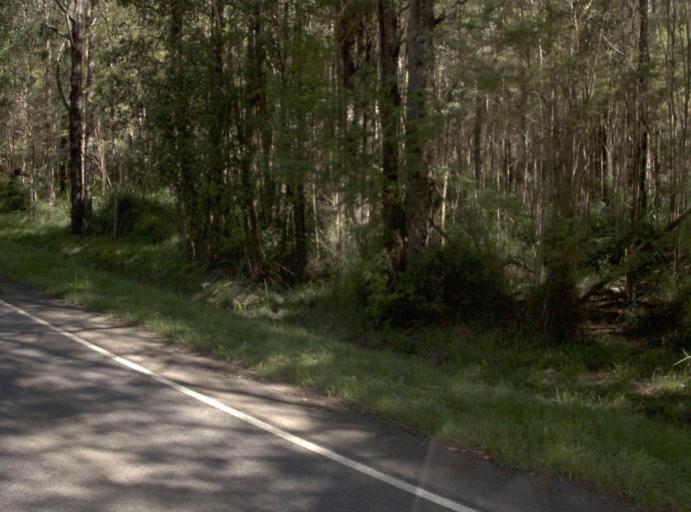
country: AU
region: Victoria
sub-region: Baw Baw
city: Warragul
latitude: -37.8881
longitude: 145.8997
